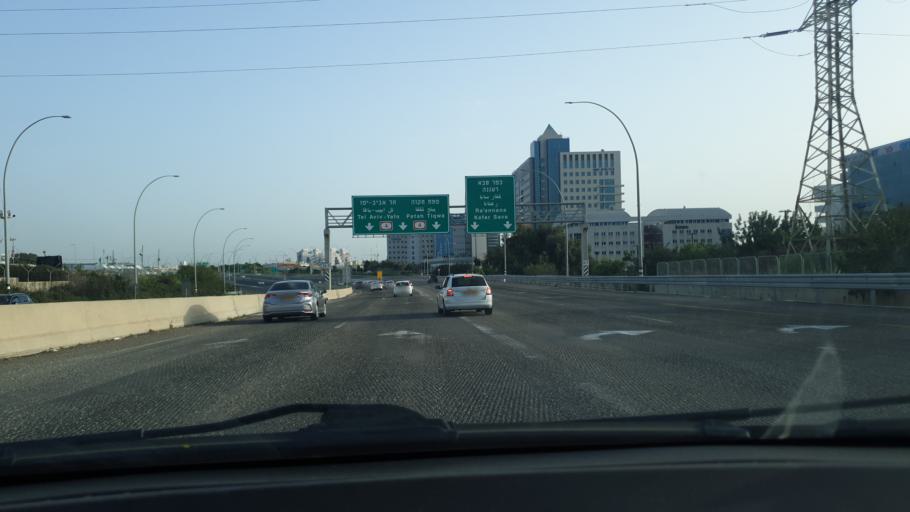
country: IL
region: Central District
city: Ra'anana
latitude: 32.1997
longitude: 34.8846
